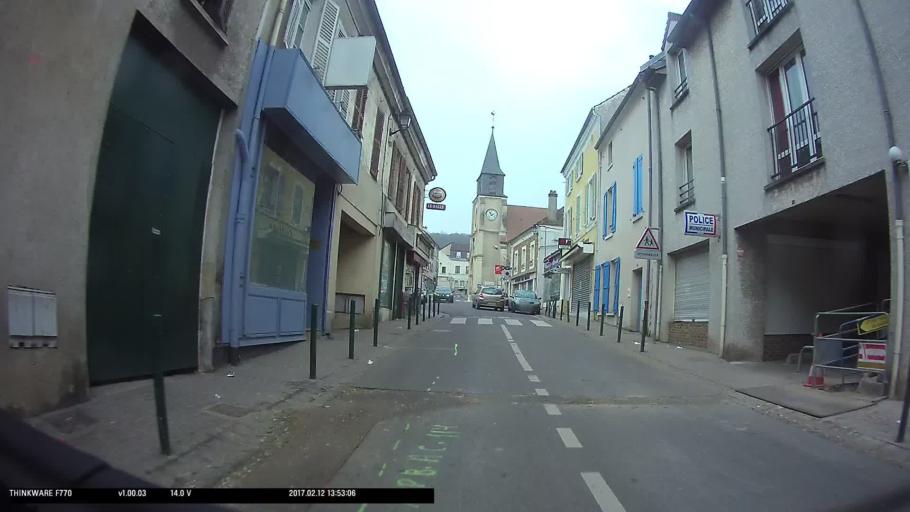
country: FR
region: Ile-de-France
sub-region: Departement des Yvelines
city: Chanteloup-les-Vignes
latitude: 48.9780
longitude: 2.0308
